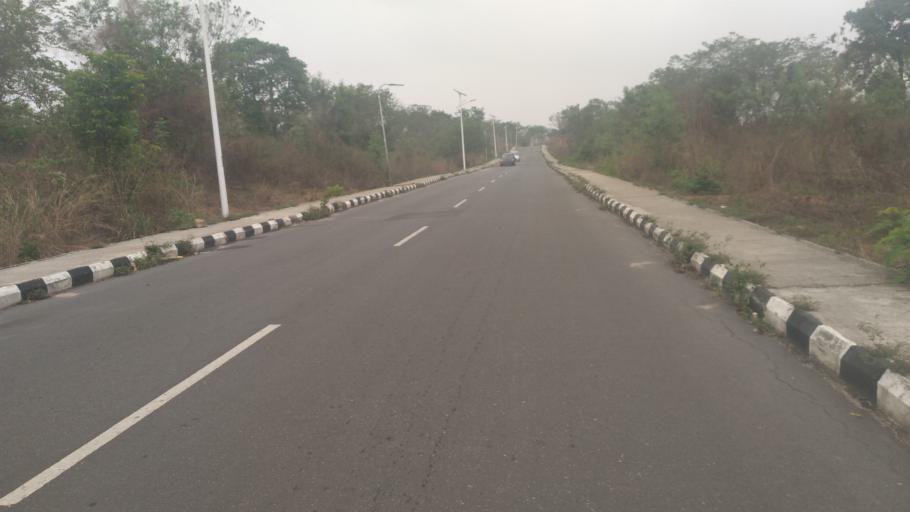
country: NG
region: Ondo
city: Ilare
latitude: 7.2952
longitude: 5.1373
